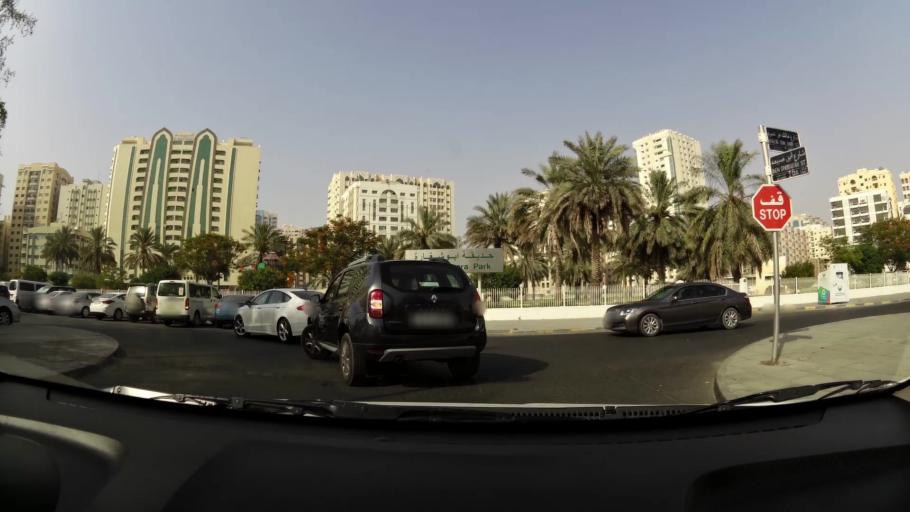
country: AE
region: Ash Shariqah
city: Sharjah
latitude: 25.3354
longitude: 55.3947
